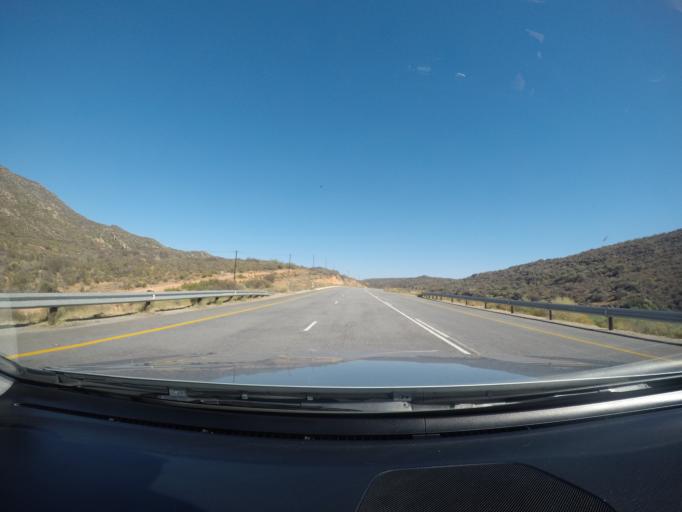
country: ZA
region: Western Cape
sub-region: West Coast District Municipality
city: Clanwilliam
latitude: -32.3423
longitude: 18.9256
